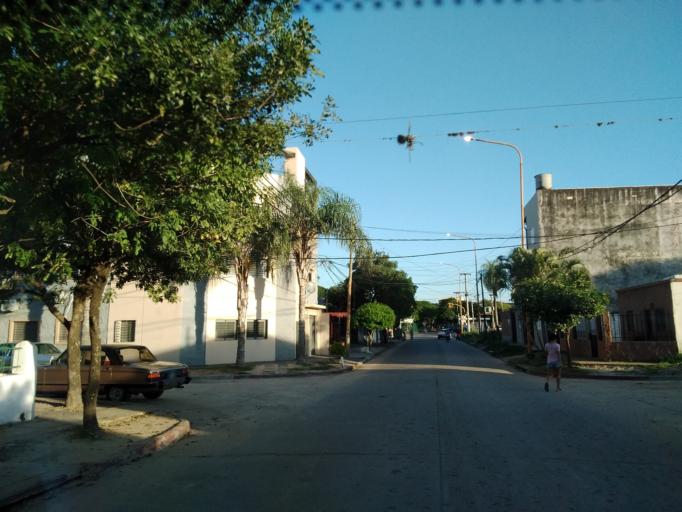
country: AR
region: Corrientes
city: Corrientes
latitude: -27.4643
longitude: -58.7843
